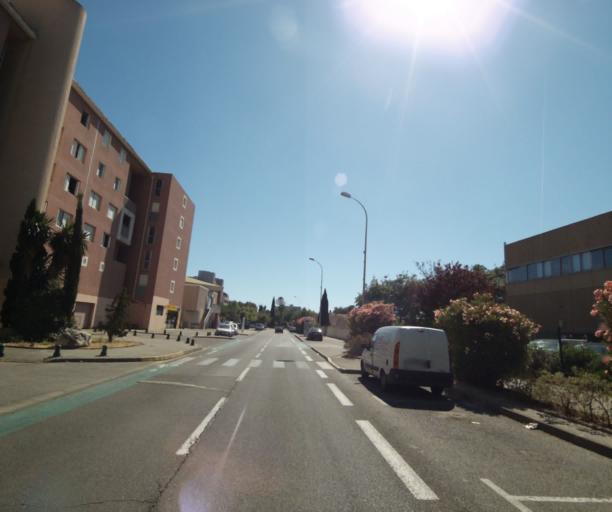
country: FR
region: Provence-Alpes-Cote d'Azur
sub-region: Departement du Var
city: La Garde
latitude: 43.1300
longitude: 6.0162
